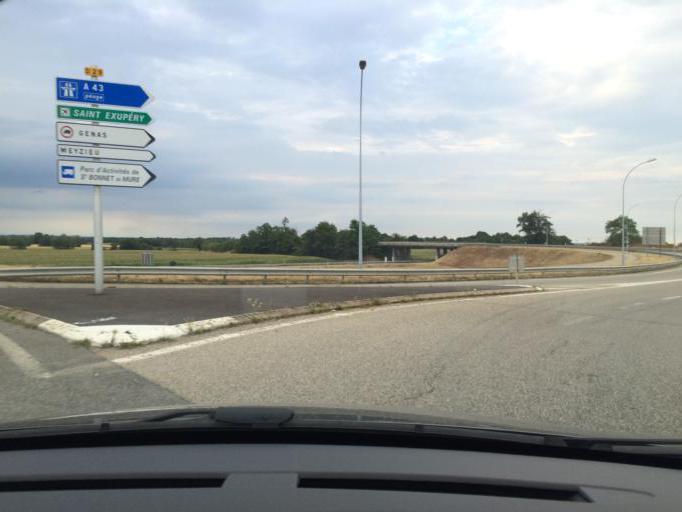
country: FR
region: Rhone-Alpes
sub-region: Departement du Rhone
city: Saint-Laurent-de-Mure
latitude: 45.6941
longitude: 5.0702
